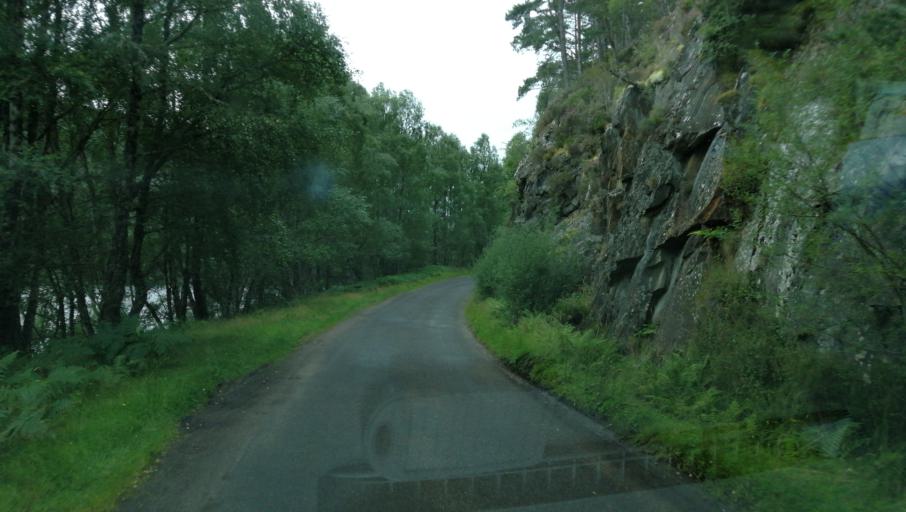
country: GB
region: Scotland
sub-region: Highland
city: Spean Bridge
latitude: 57.3034
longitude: -4.8742
